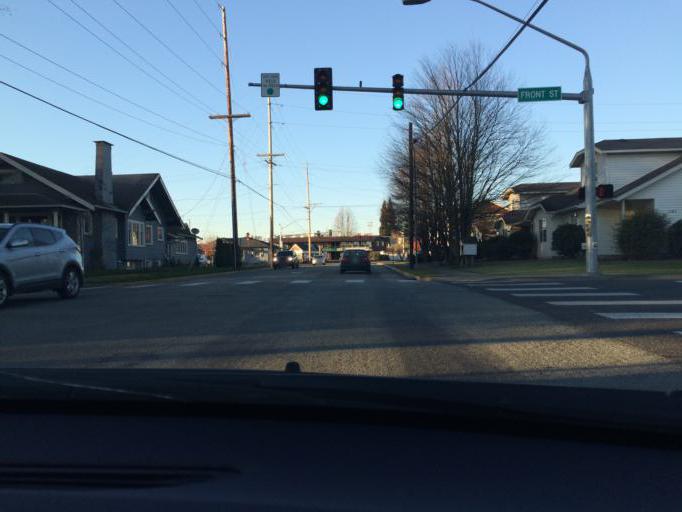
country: US
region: Washington
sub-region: Whatcom County
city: Lynden
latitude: 48.9442
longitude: -122.4480
